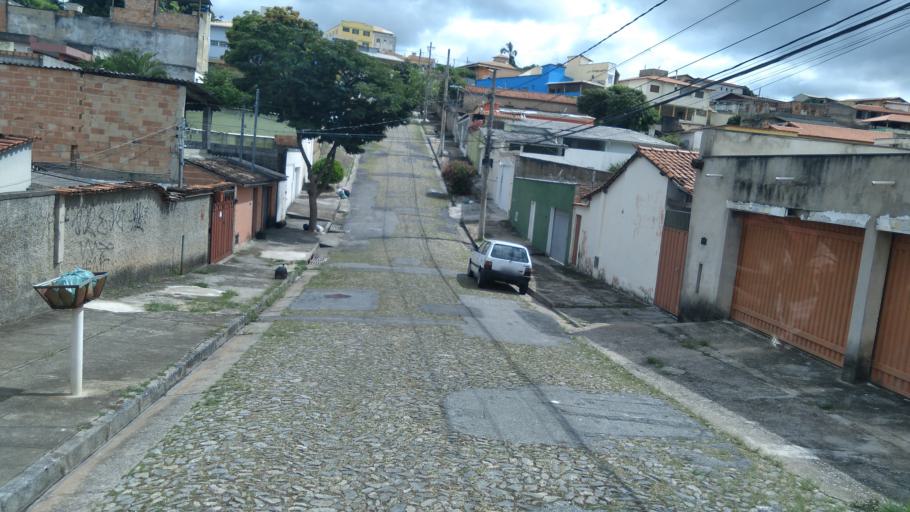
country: BR
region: Minas Gerais
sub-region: Belo Horizonte
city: Belo Horizonte
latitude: -19.8872
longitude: -43.9003
